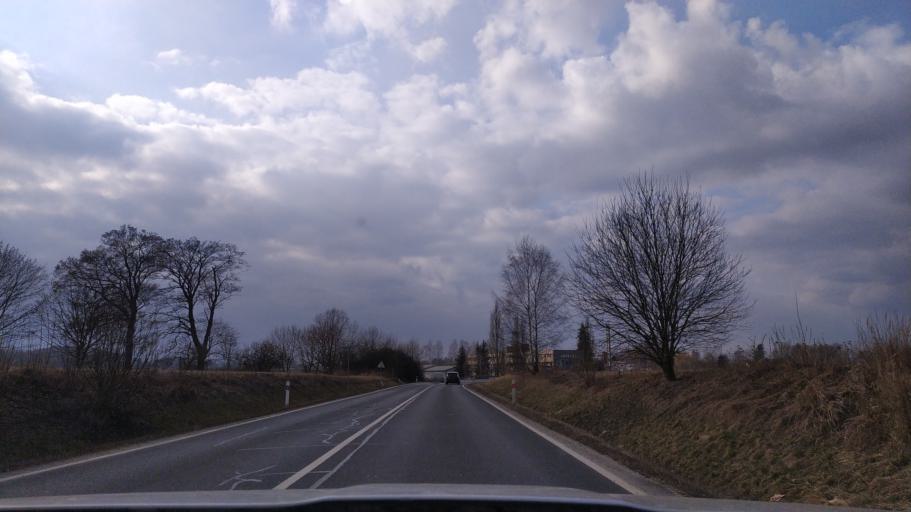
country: CZ
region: Karlovarsky
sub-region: Okres Cheb
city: Frantiskovy Lazne
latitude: 50.1071
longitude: 12.3603
